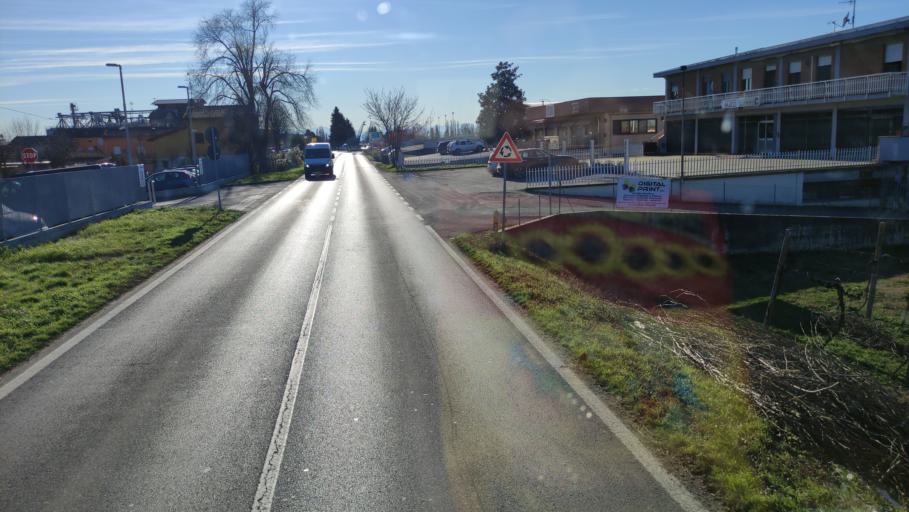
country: IT
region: Emilia-Romagna
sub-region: Provincia di Reggio Emilia
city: Novellara
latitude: 44.8369
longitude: 10.7146
